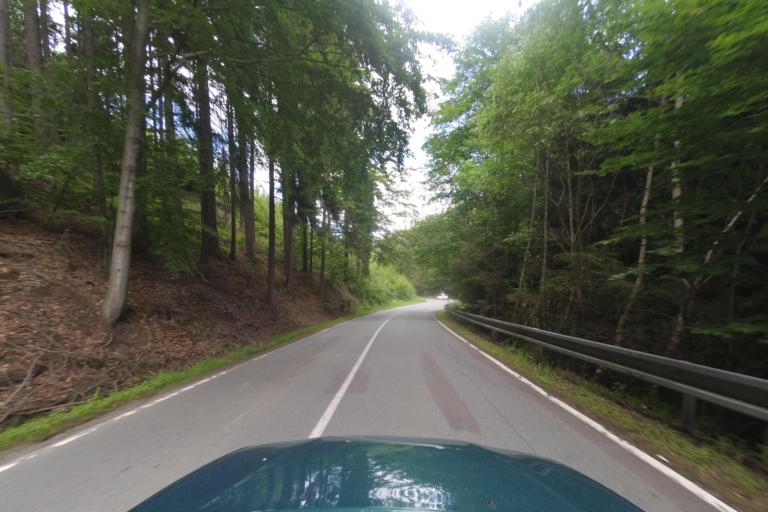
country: PL
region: Lower Silesian Voivodeship
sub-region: Powiat klodzki
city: Lewin Klodzki
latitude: 50.3479
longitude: 16.2403
